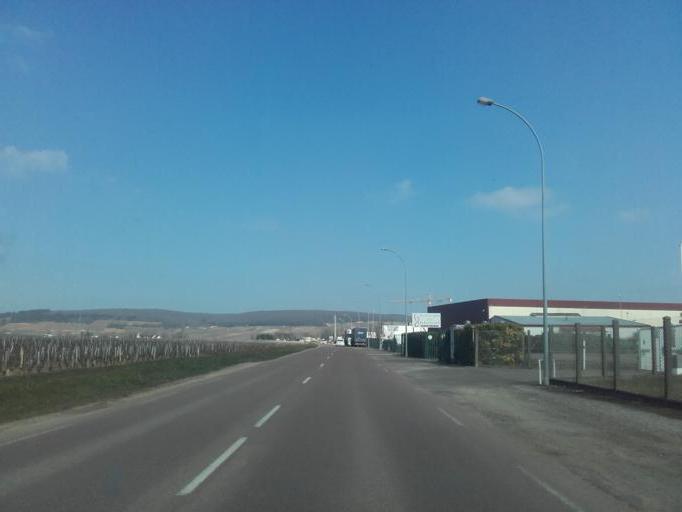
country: FR
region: Bourgogne
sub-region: Departement de la Cote-d'Or
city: Beaune
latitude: 47.0475
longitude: 4.8395
